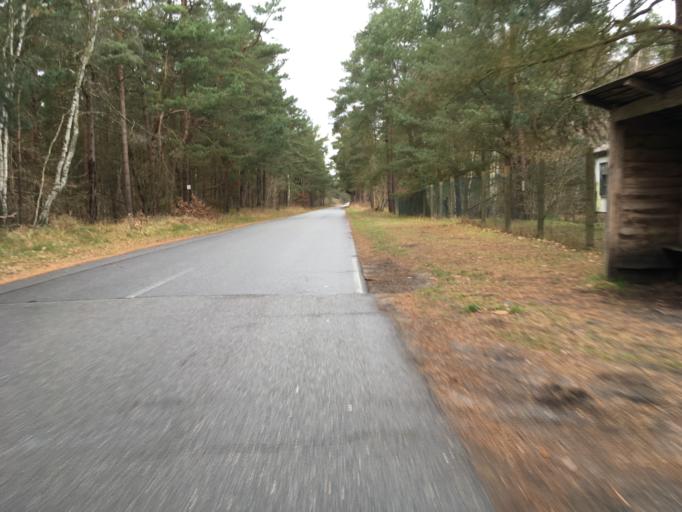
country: DE
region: Mecklenburg-Vorpommern
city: Ostseebad Binz
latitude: 54.4520
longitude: 13.5644
